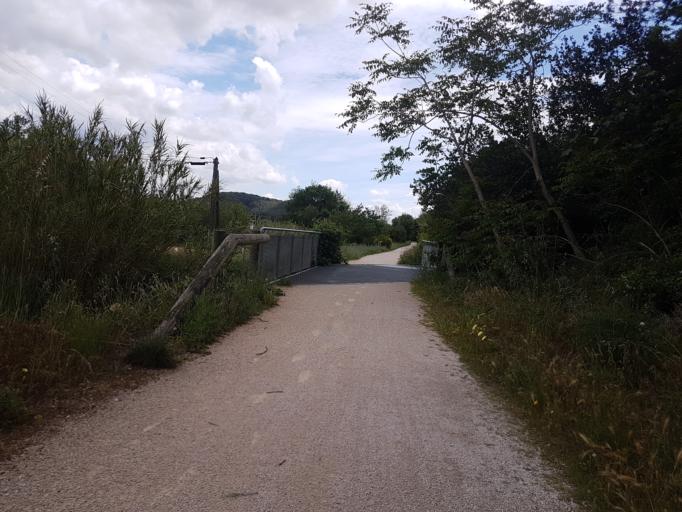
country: FR
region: Languedoc-Roussillon
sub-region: Departement du Gard
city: Beaucaire
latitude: 43.8255
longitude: 4.6265
